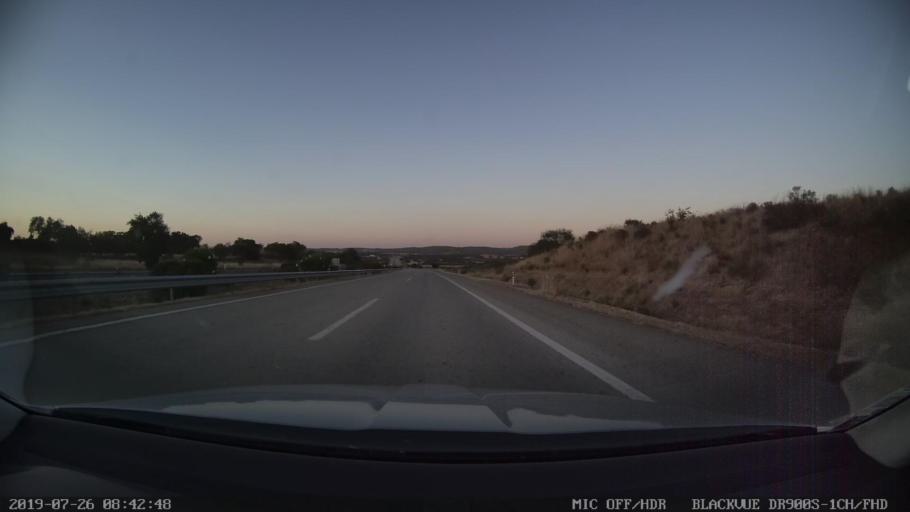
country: PT
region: Evora
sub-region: Montemor-O-Novo
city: Montemor-o-Novo
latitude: 38.6509
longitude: -8.2515
